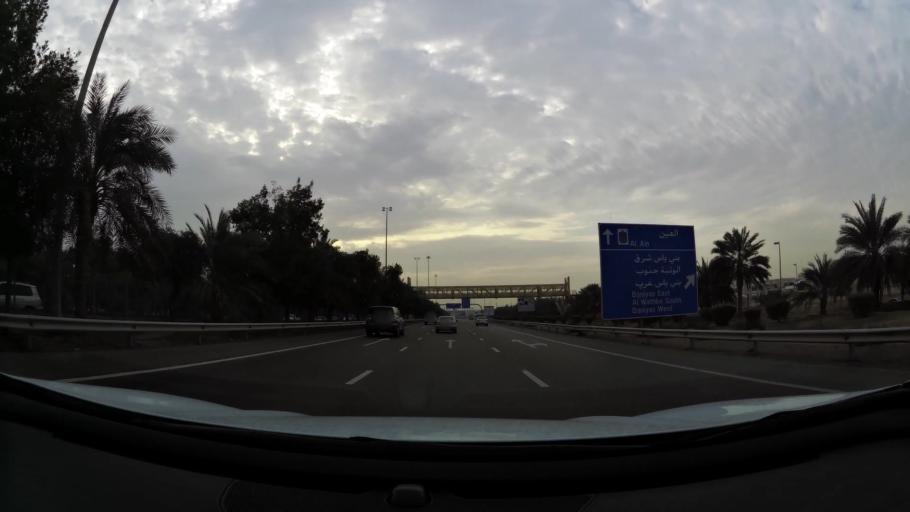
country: AE
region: Abu Dhabi
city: Abu Dhabi
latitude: 24.2846
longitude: 54.6430
